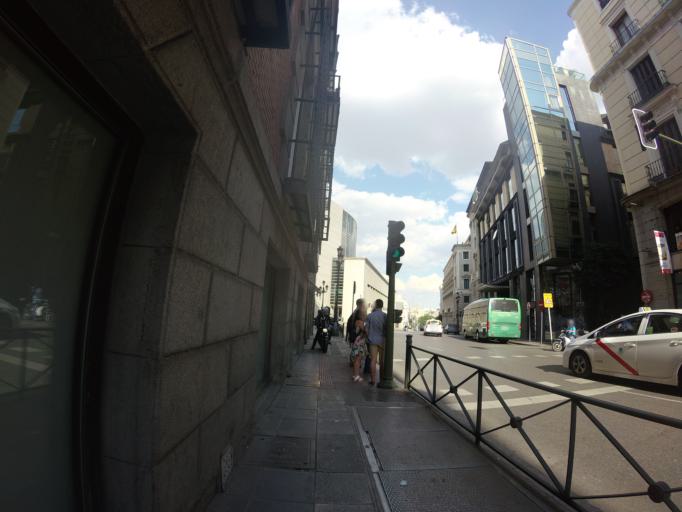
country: ES
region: Madrid
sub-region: Provincia de Madrid
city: Madrid
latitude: 40.4166
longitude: -3.6989
